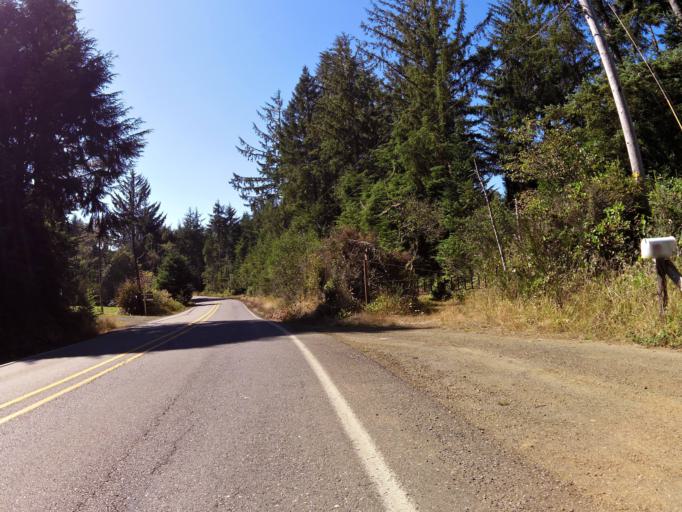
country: US
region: Oregon
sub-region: Coos County
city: Barview
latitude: 43.3297
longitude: -124.3397
